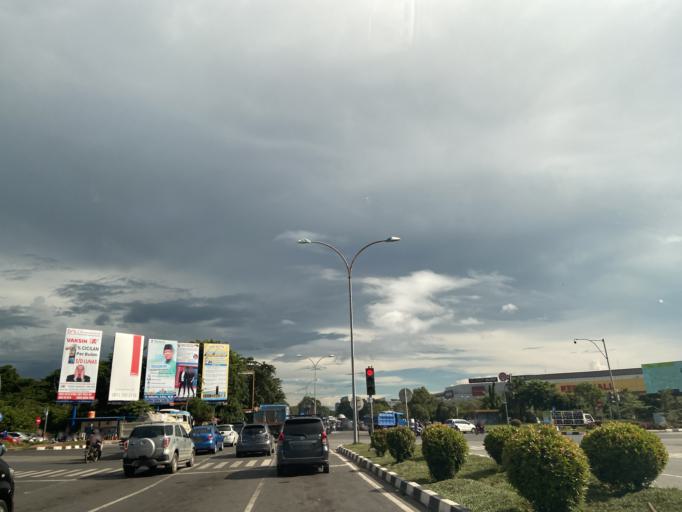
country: SG
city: Singapore
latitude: 1.1028
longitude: 104.0391
